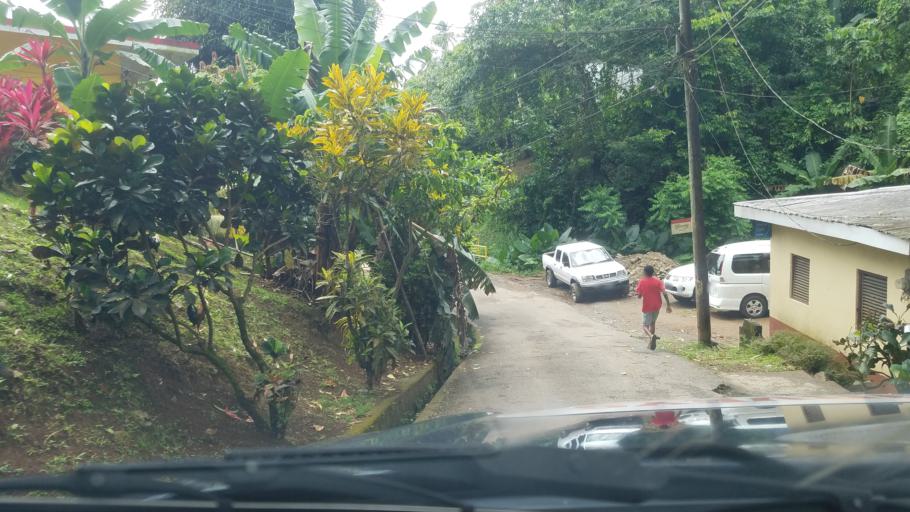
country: LC
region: Castries Quarter
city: Bisee
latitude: 14.0015
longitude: -60.9752
